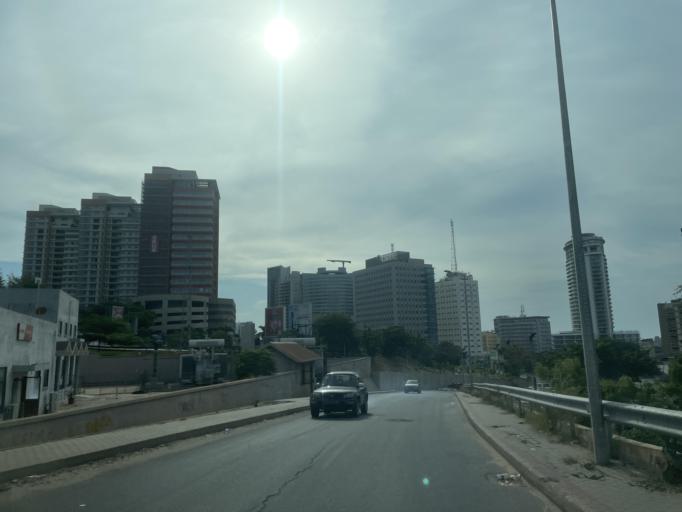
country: AO
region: Luanda
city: Luanda
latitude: -8.8100
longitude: 13.2431
